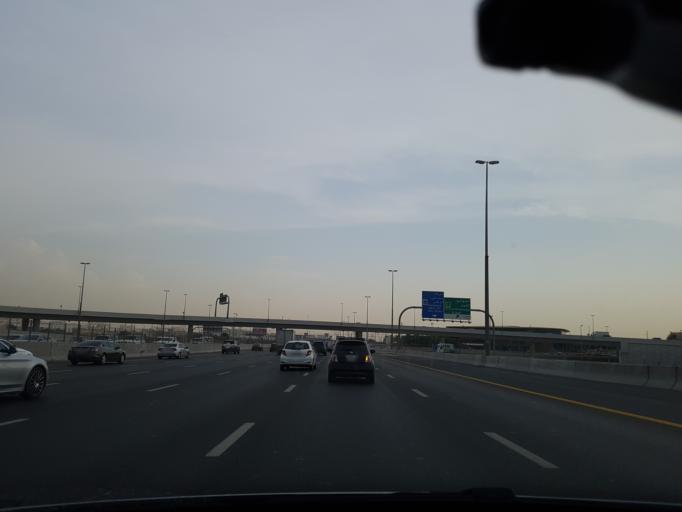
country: AE
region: Ash Shariqah
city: Sharjah
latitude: 25.2326
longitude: 55.4041
